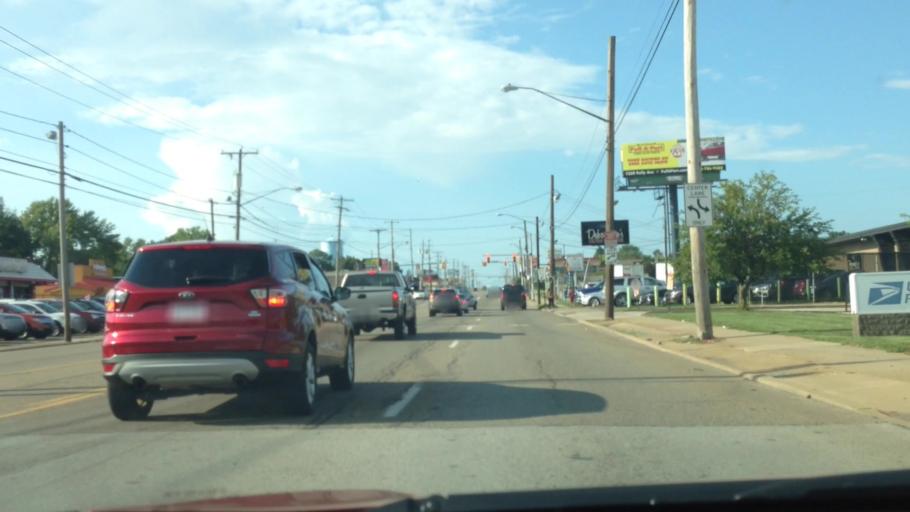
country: US
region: Ohio
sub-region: Summit County
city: Portage Lakes
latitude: 41.0382
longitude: -81.4912
